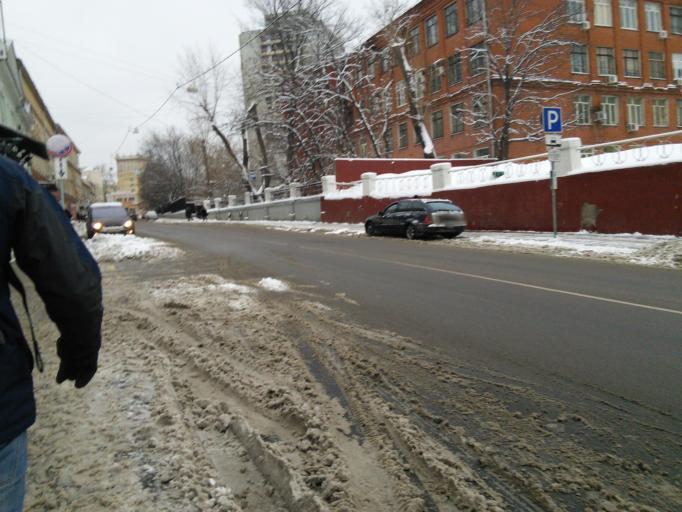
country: RU
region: Moscow
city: Taganskiy
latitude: 55.7624
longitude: 37.6629
